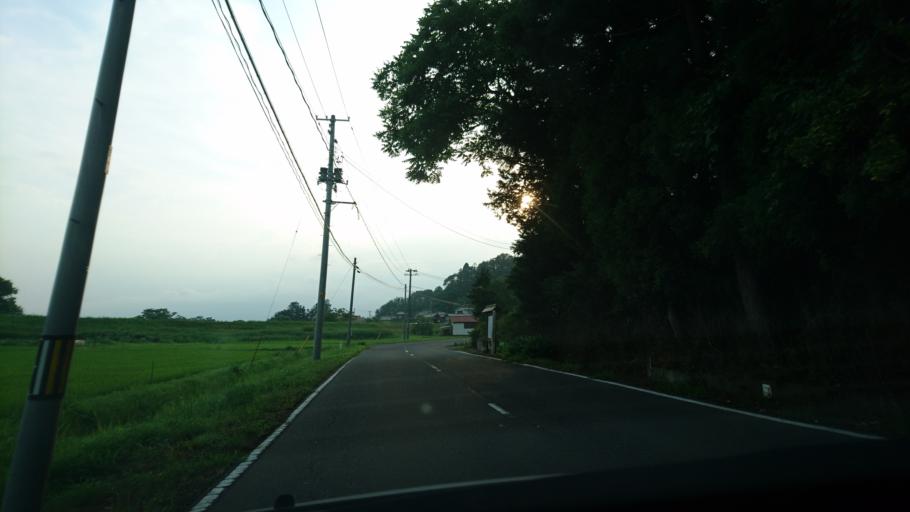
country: JP
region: Iwate
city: Ichinoseki
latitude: 38.7804
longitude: 141.0484
